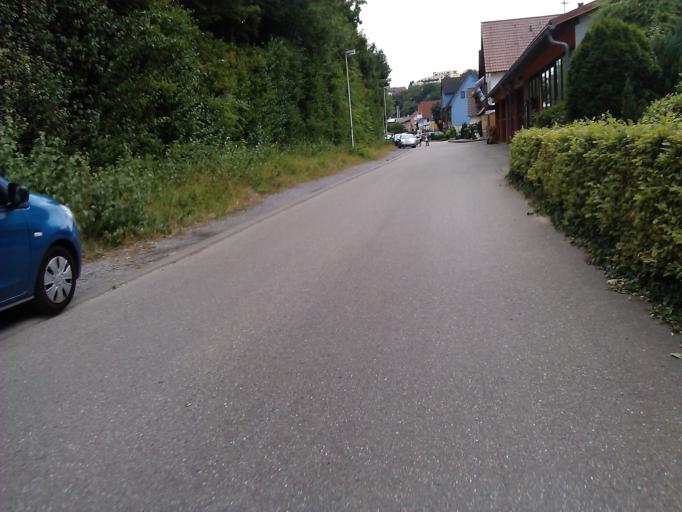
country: DE
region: Baden-Wuerttemberg
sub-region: Regierungsbezirk Stuttgart
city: Talheim
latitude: 49.0882
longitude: 9.1906
